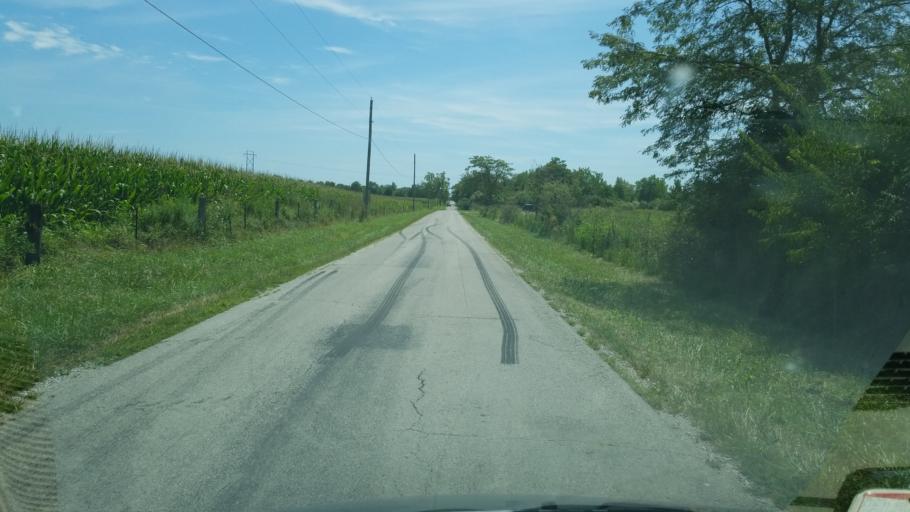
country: US
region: Ohio
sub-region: Franklin County
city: Lake Darby
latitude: 39.8683
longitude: -83.2031
